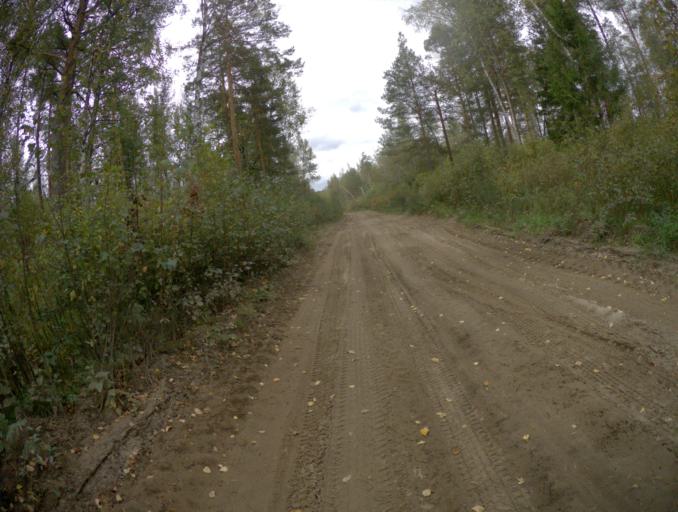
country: RU
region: Vladimir
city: Petushki
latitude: 55.8338
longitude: 39.5354
